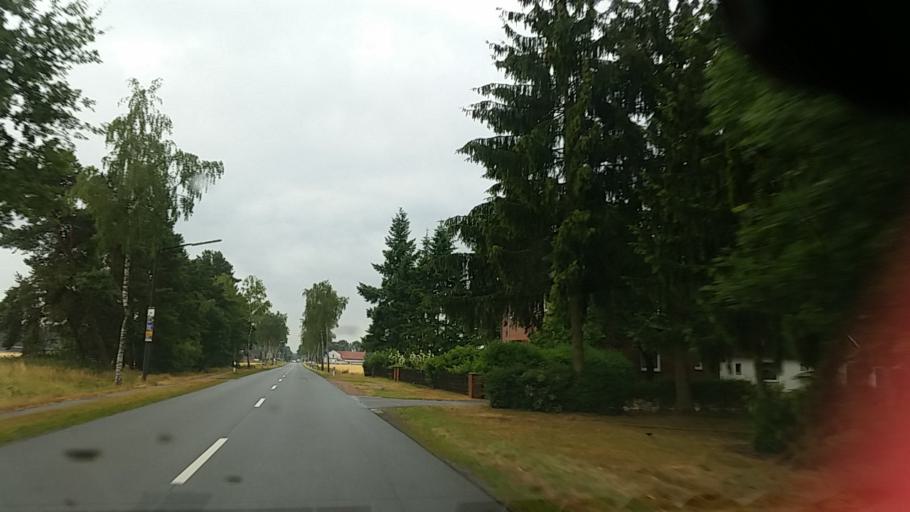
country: DE
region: Lower Saxony
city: Schoneworde
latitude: 52.6280
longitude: 10.6898
